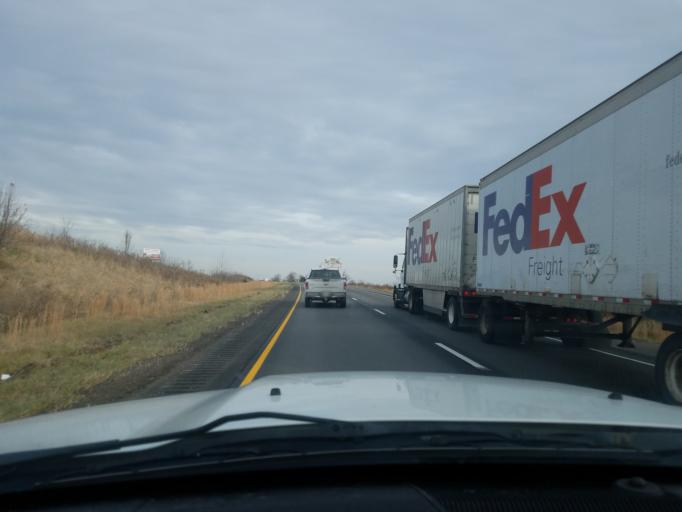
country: US
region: Indiana
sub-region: Dubois County
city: Ferdinand
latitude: 38.2020
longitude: -86.8327
